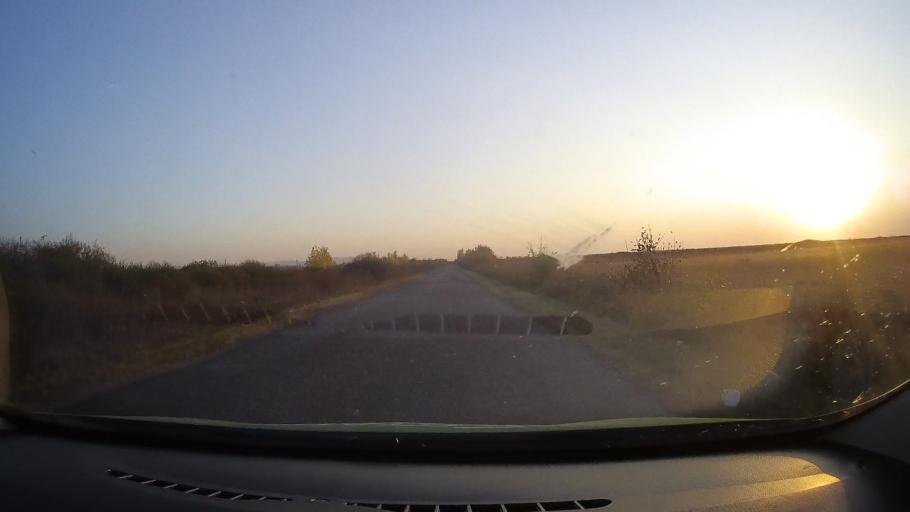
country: RO
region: Arad
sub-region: Comuna Sicula
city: Sicula
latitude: 46.4102
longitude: 21.7329
